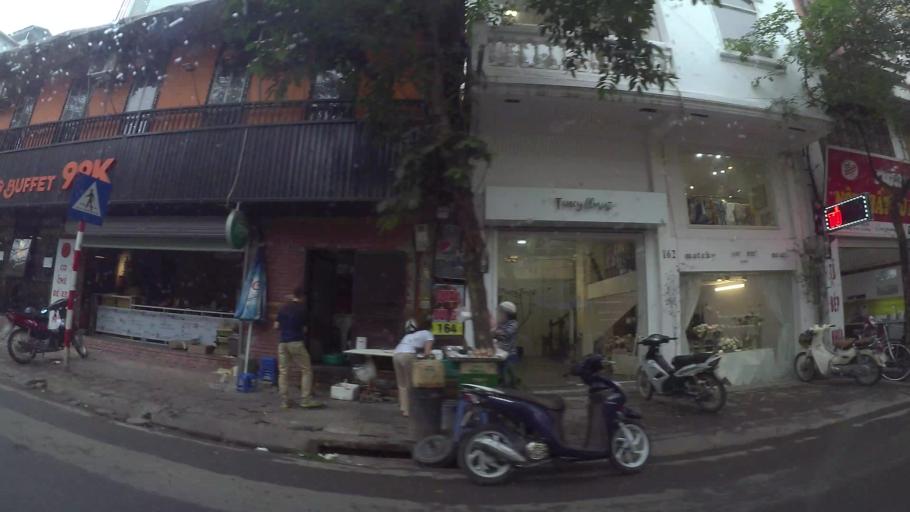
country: VN
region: Ha Noi
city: Dong Da
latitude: 21.0128
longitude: 105.8166
